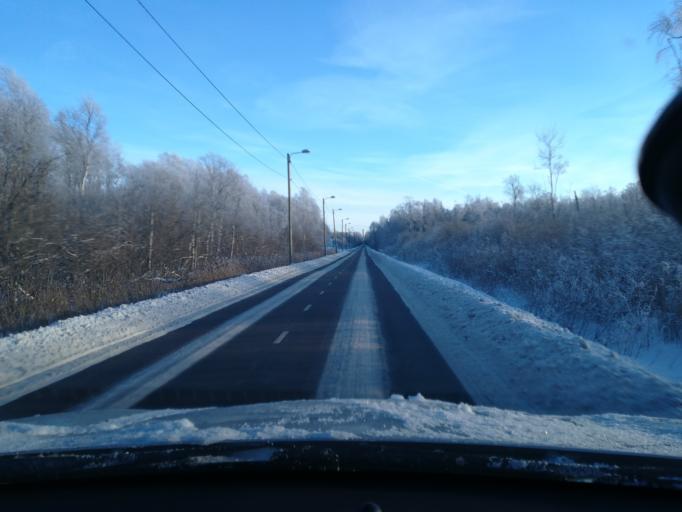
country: EE
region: Harju
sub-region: Saue vald
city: Laagri
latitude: 59.3930
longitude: 24.6035
